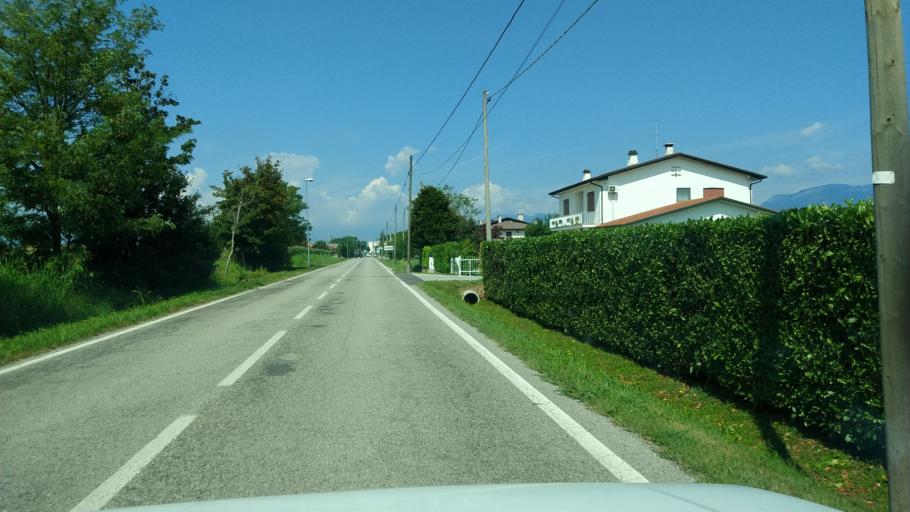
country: IT
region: Veneto
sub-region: Provincia di Vicenza
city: Schiavon
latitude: 45.6914
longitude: 11.6498
